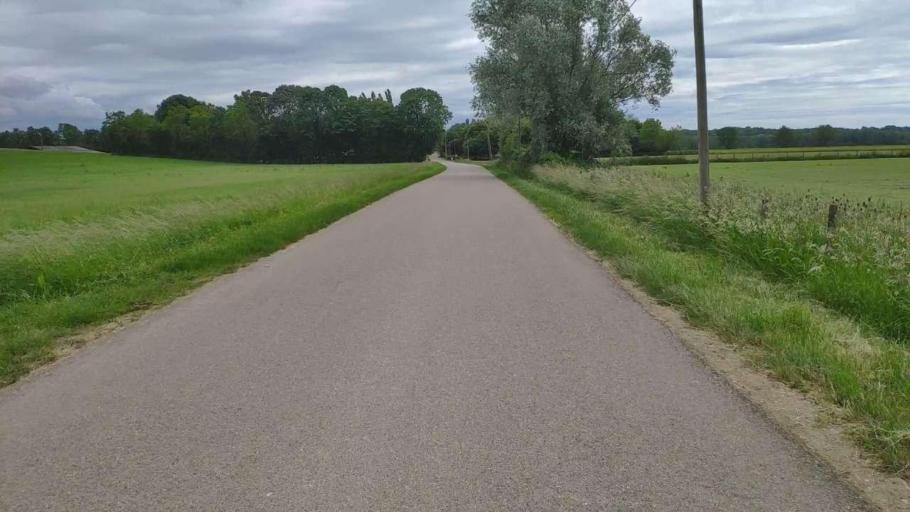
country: FR
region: Franche-Comte
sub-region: Departement du Jura
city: Bletterans
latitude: 46.7333
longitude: 5.4977
